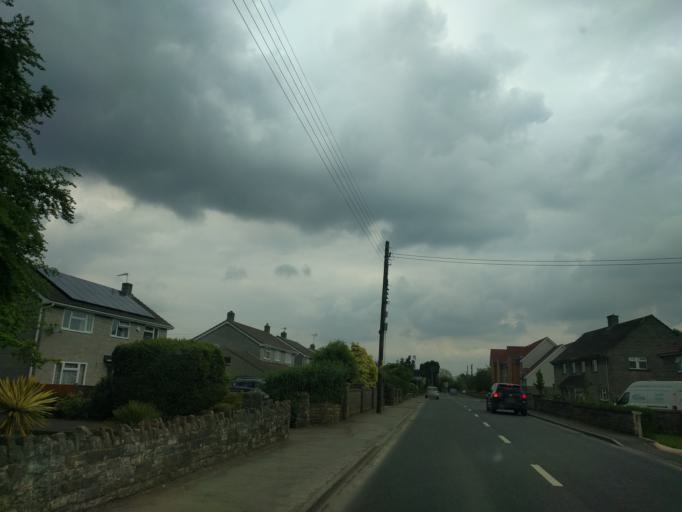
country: GB
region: England
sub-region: Somerset
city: Street
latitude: 51.0558
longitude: -2.7327
